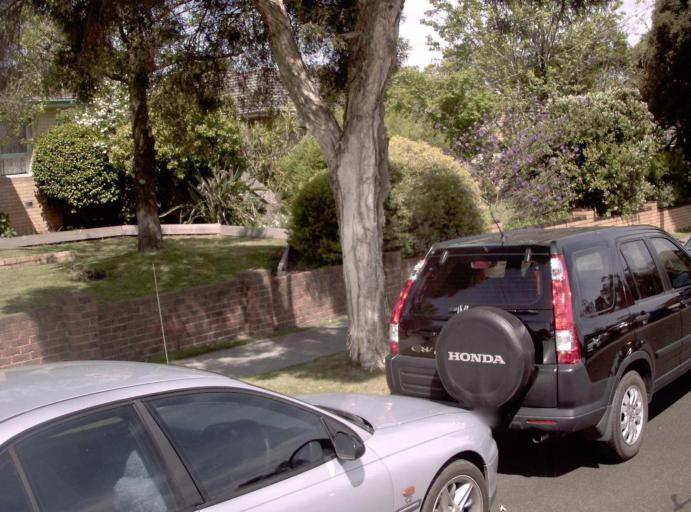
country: AU
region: Victoria
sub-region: Maroondah
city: Croydon Hills
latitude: -37.7846
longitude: 145.2693
